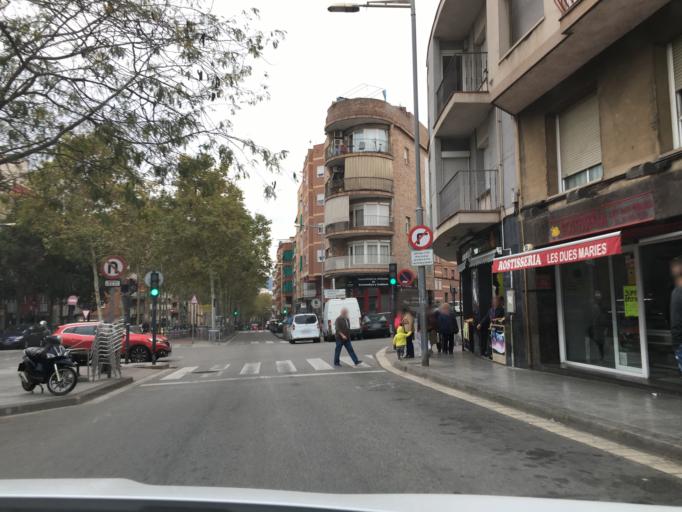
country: ES
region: Catalonia
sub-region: Provincia de Barcelona
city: Santa Coloma de Gramenet
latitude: 41.4513
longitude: 2.2162
